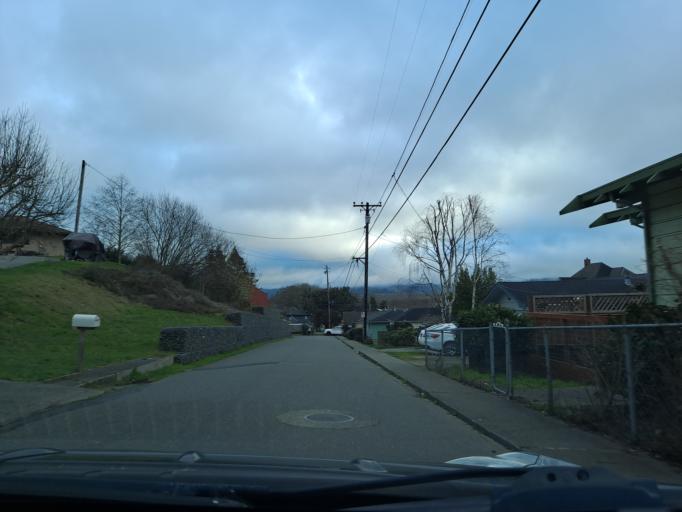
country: US
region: California
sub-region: Humboldt County
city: Fortuna
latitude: 40.6010
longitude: -124.1609
